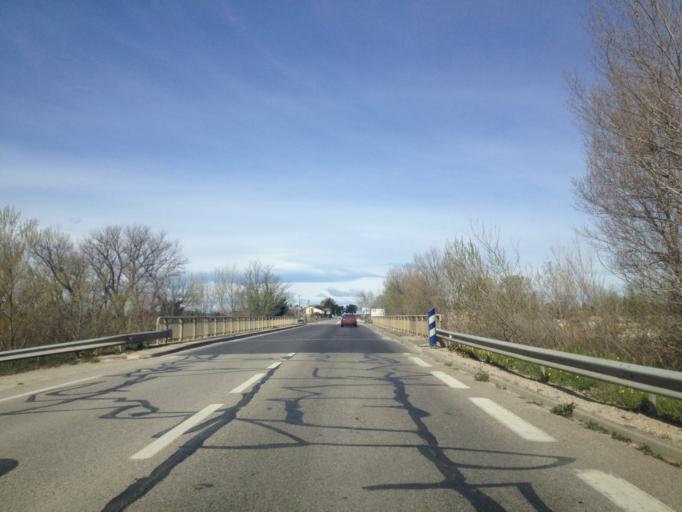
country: FR
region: Provence-Alpes-Cote d'Azur
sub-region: Departement du Vaucluse
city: Sablet
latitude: 44.1942
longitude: 4.9848
